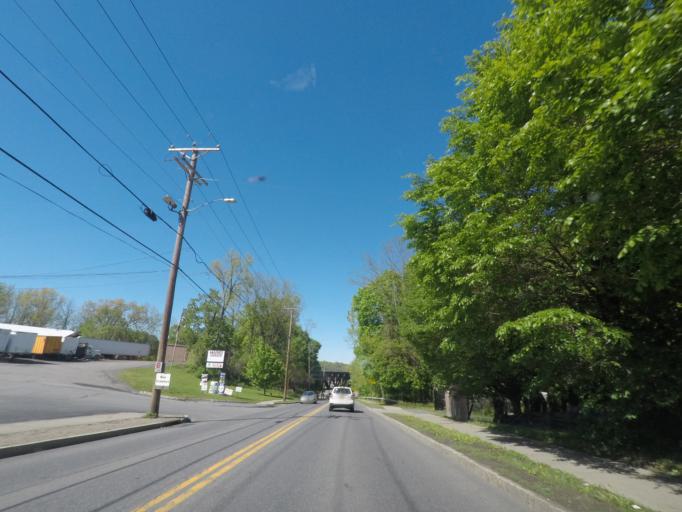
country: US
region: New York
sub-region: Greene County
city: Catskill
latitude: 42.2206
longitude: -73.8726
